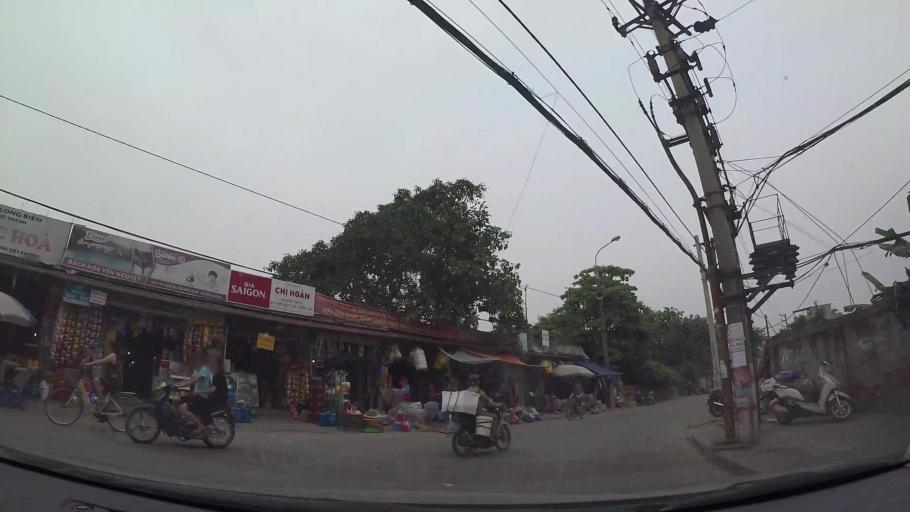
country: VN
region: Ha Noi
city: Hoan Kiem
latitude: 21.0695
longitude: 105.8880
